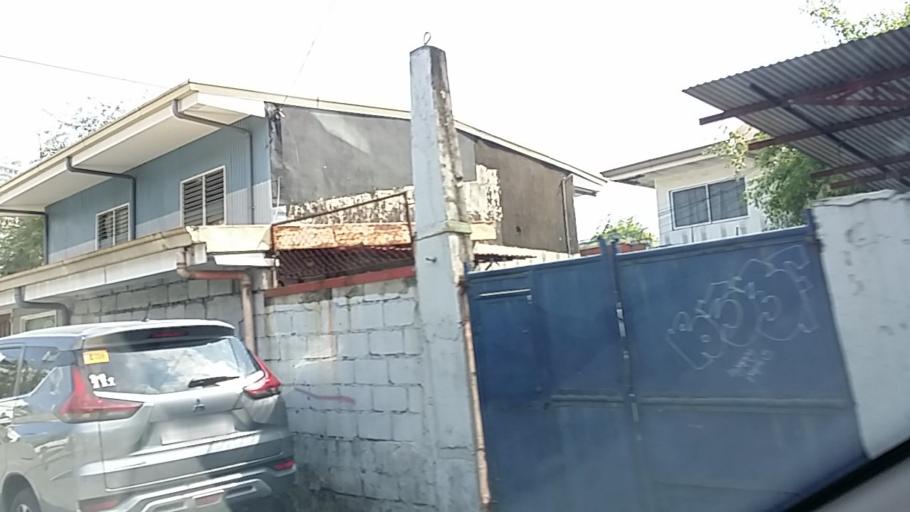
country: PH
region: Metro Manila
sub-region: Mandaluyong
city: Mandaluyong City
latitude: 14.5735
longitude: 121.0343
